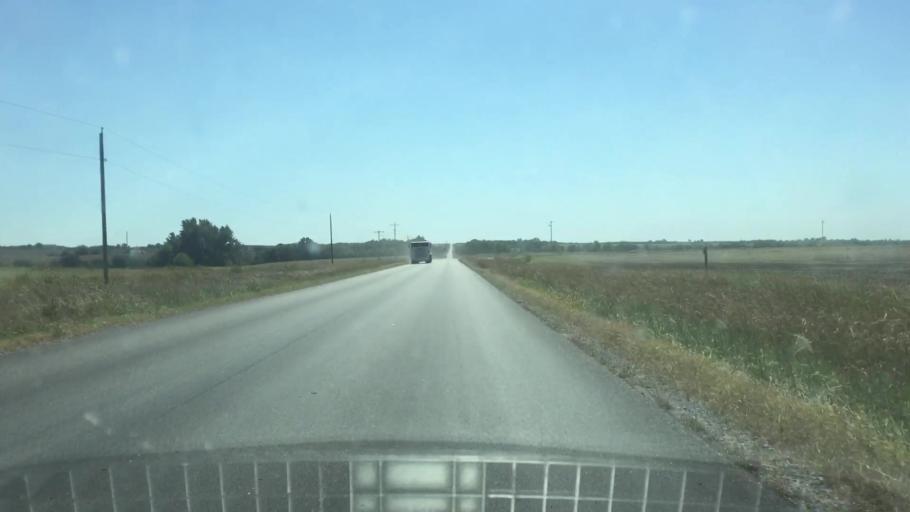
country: US
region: Kansas
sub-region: Marshall County
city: Marysville
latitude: 39.9457
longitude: -96.6009
